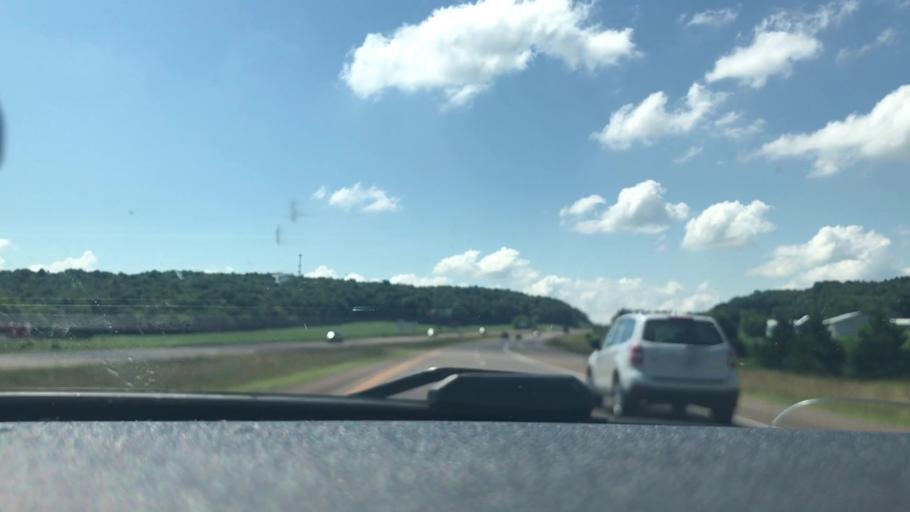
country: US
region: Wisconsin
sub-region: Chippewa County
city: Chippewa Falls
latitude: 44.9632
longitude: -91.4261
